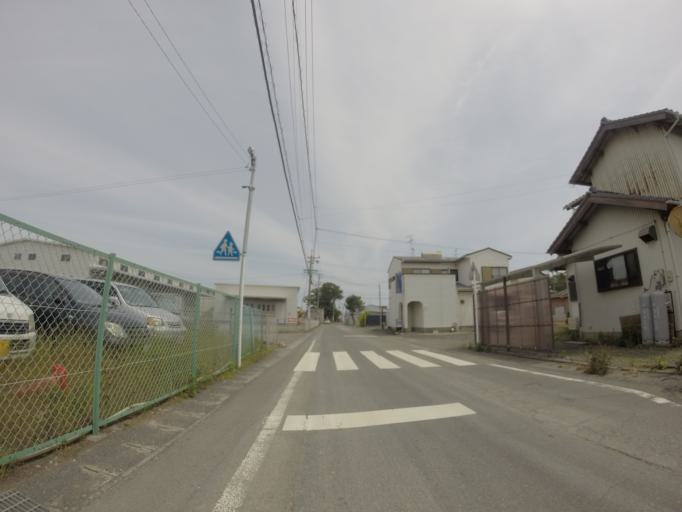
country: JP
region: Shizuoka
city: Yaizu
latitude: 34.8016
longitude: 138.3136
